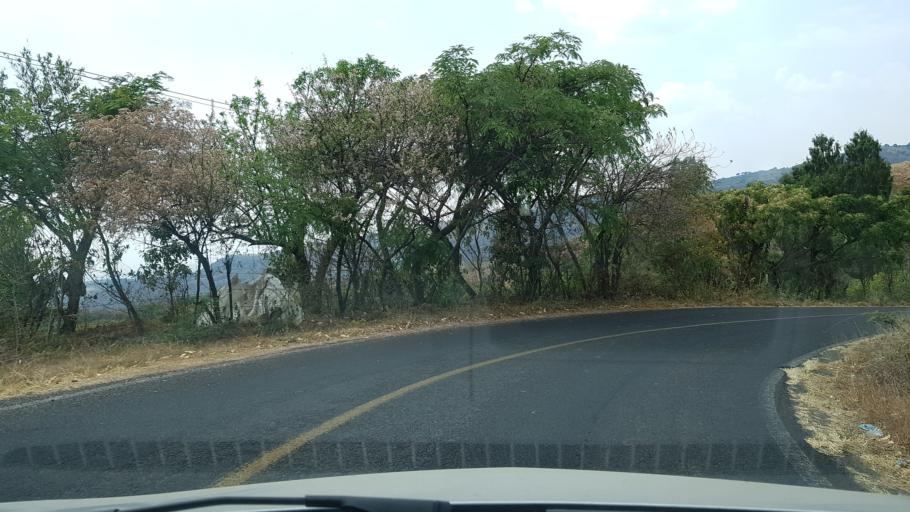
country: MX
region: Morelos
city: Tlacotepec
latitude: 18.8352
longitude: -98.7246
